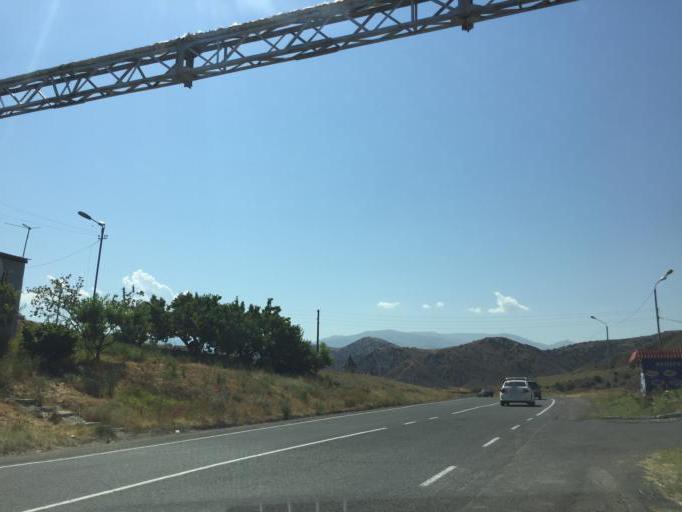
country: AM
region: Vayots' Dzori Marz
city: Vayk'
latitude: 39.7021
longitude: 45.4378
